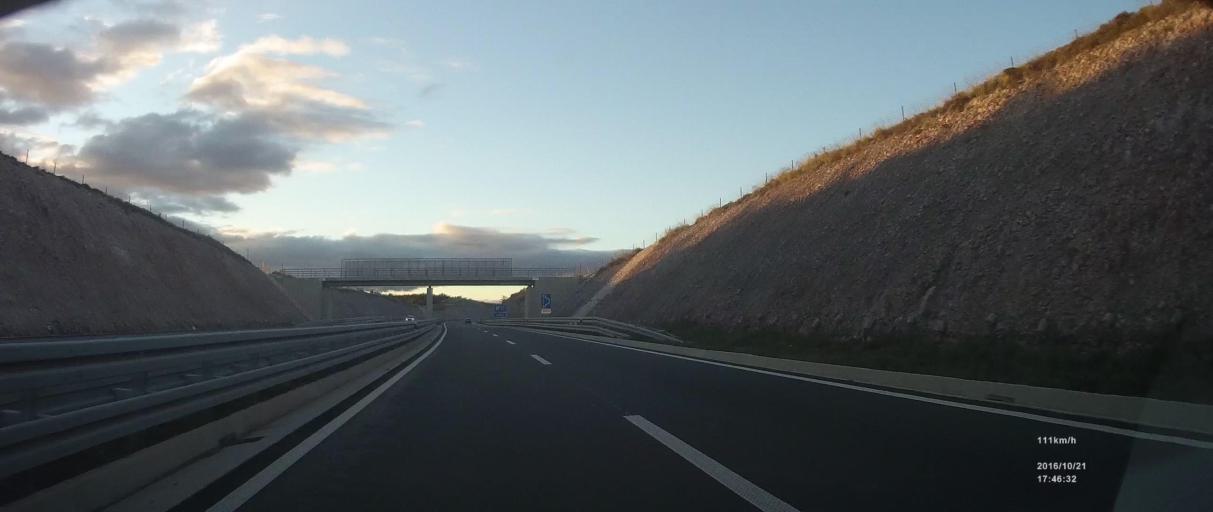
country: HR
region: Primorsko-Goranska
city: Krasica
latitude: 45.3026
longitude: 14.5592
